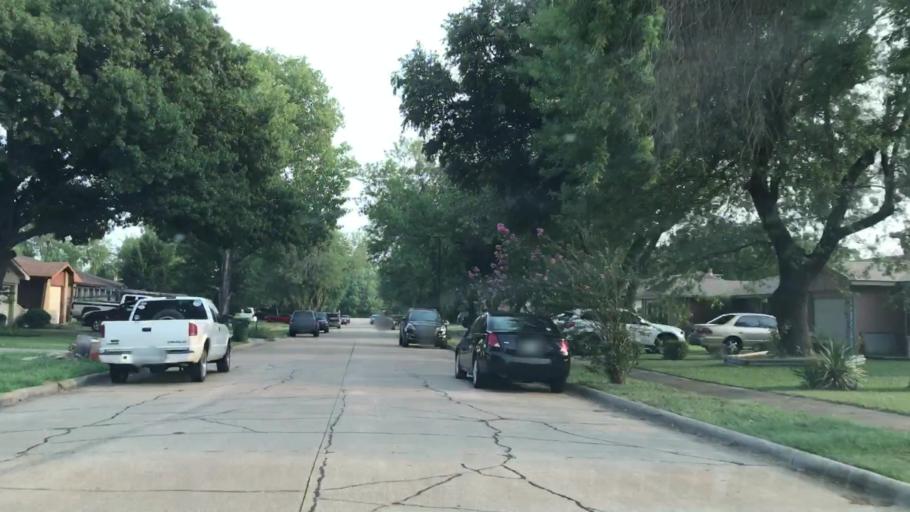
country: US
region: Texas
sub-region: Dallas County
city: Garland
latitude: 32.9242
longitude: -96.6105
